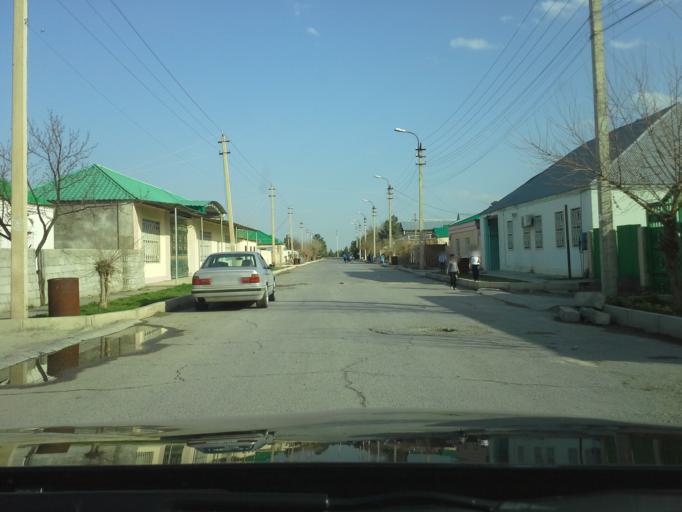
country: TM
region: Ahal
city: Abadan
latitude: 38.0179
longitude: 58.2344
